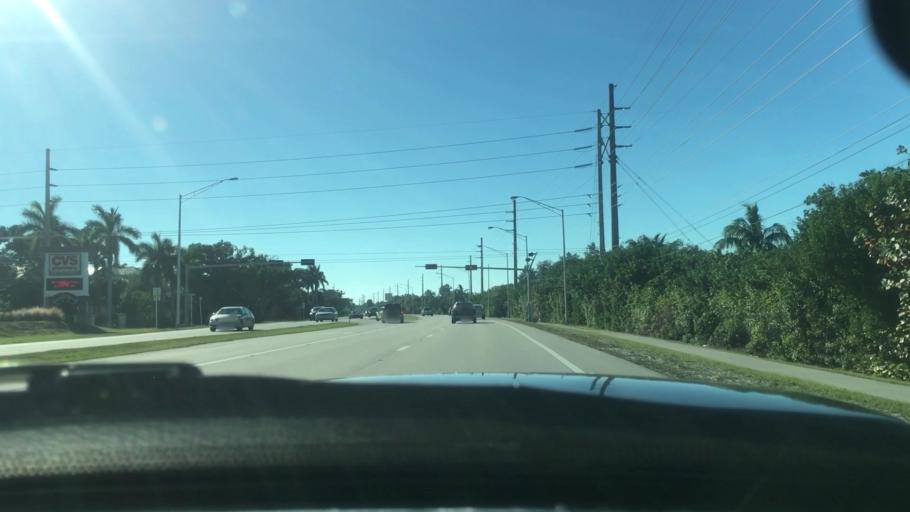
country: US
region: Florida
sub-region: Monroe County
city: Stock Island
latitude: 24.5747
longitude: -81.7368
